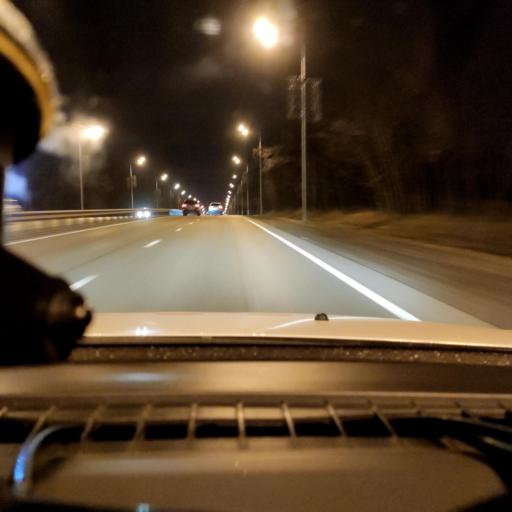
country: RU
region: Samara
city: Novosemeykino
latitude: 53.3232
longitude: 50.2305
